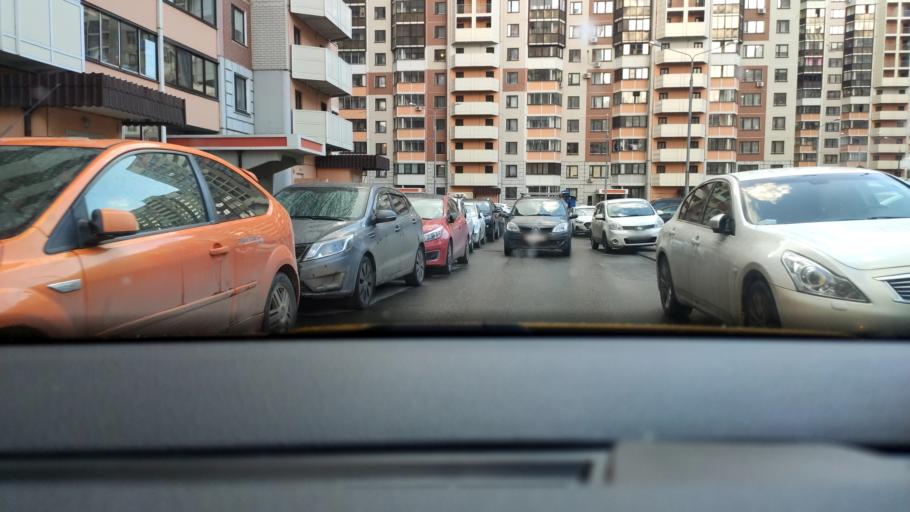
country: RU
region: Moskovskaya
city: Zheleznodorozhnyy
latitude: 55.7392
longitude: 37.9840
